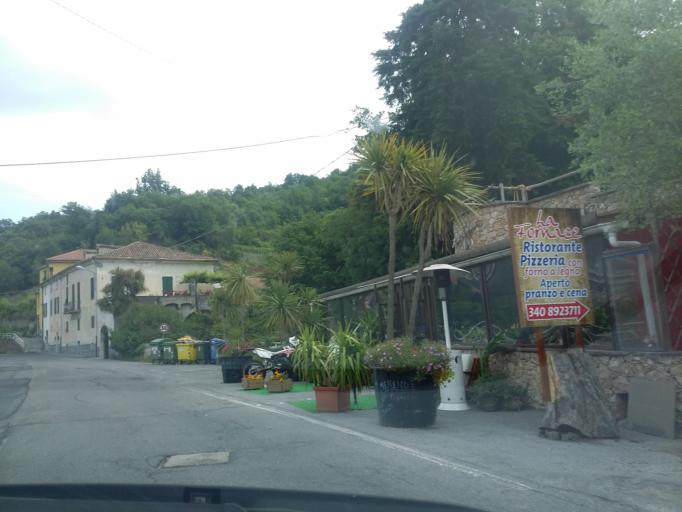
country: IT
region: Liguria
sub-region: Provincia di Savona
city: Feglino
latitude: 44.2161
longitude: 8.3259
